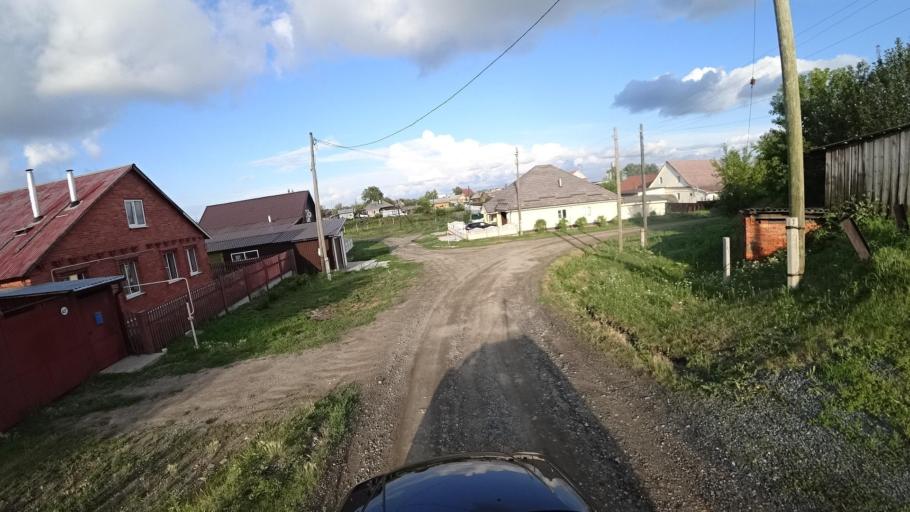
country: RU
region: Sverdlovsk
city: Kamyshlov
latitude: 56.8507
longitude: 62.6704
